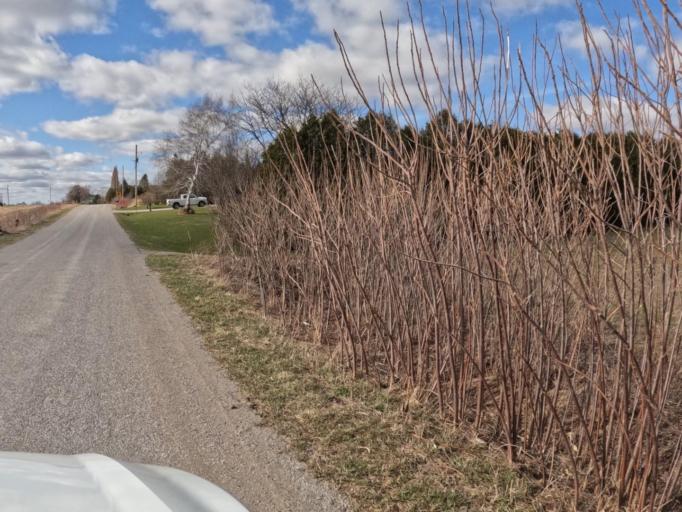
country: CA
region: Ontario
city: Norfolk County
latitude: 42.7531
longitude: -80.3017
